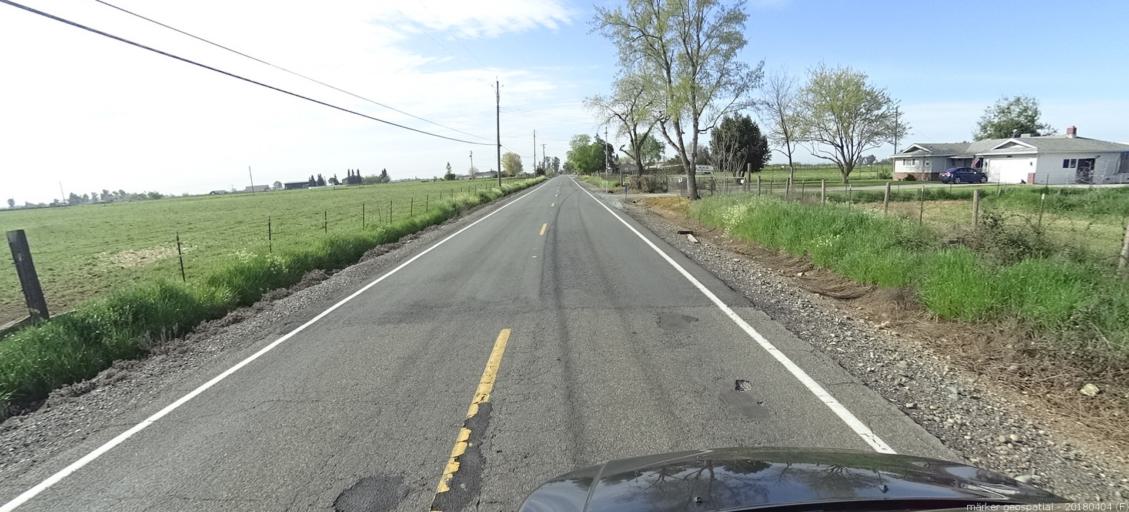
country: US
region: California
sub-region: Sacramento County
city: Herald
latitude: 38.2725
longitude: -121.2266
